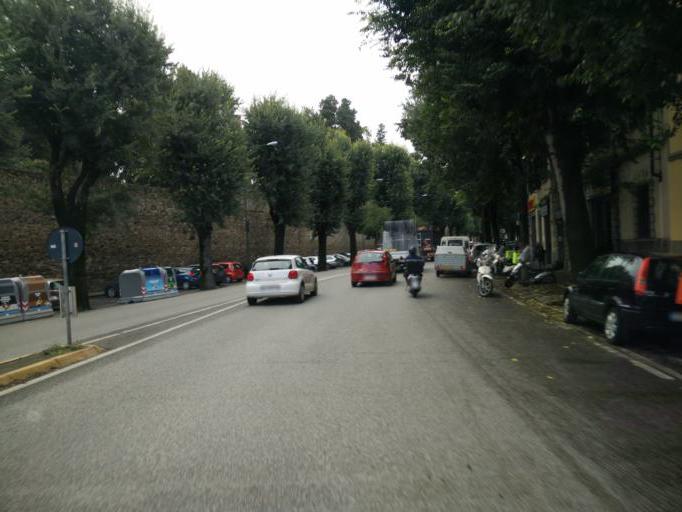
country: IT
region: Tuscany
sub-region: Province of Florence
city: Florence
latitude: 43.7667
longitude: 11.2405
